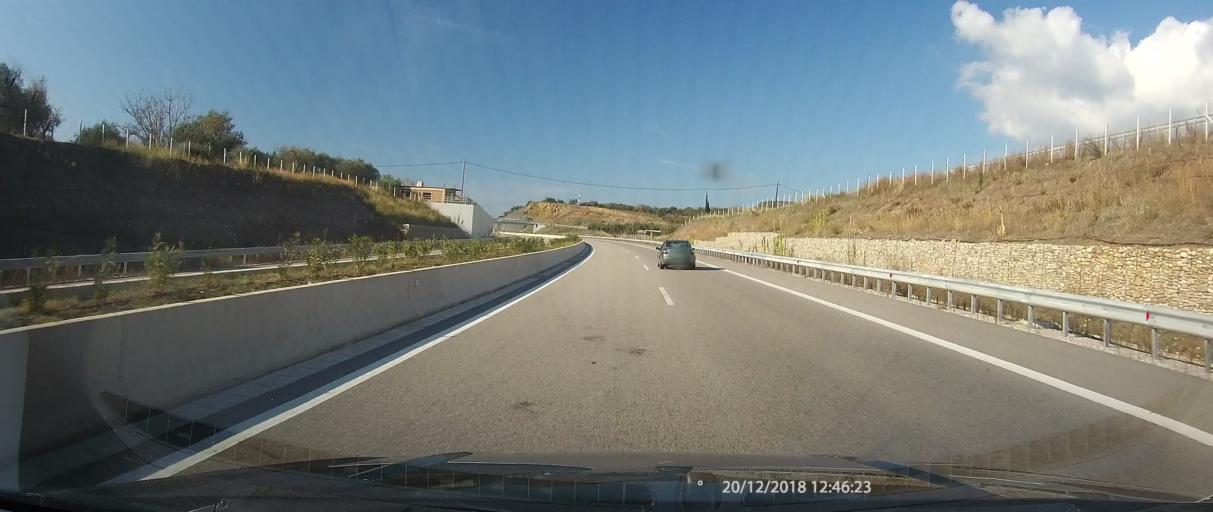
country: GR
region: West Greece
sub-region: Nomos Aitolias kai Akarnanias
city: Mesolongi
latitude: 38.3918
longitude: 21.4749
